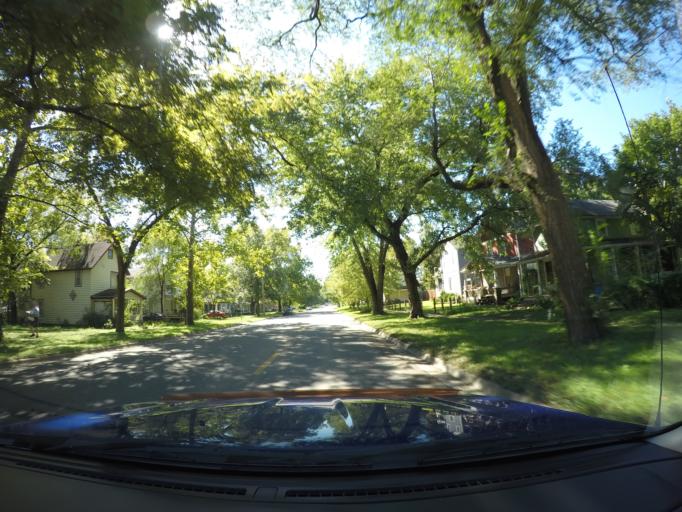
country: US
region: Kansas
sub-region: Douglas County
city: Lawrence
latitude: 38.9598
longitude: -95.2325
